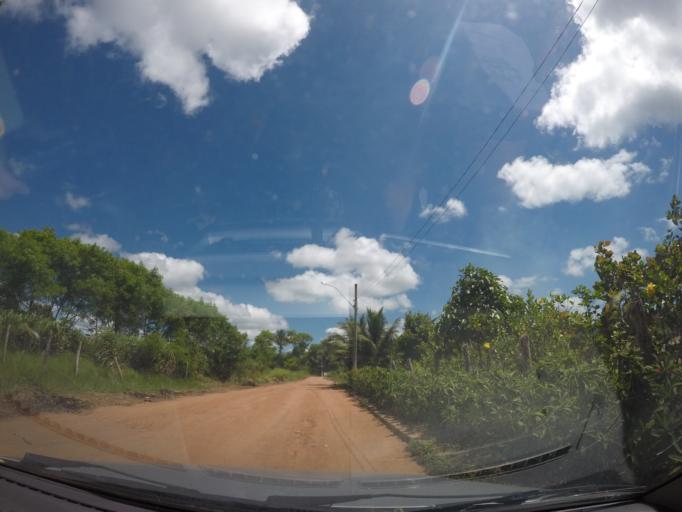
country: BR
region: Espirito Santo
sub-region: Serra
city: Serra
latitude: -20.0116
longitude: -40.1575
